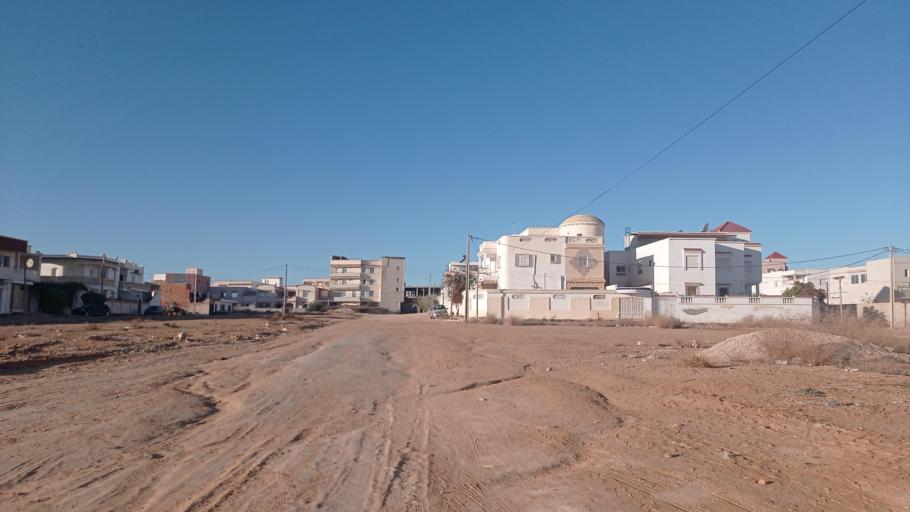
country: TN
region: Qabis
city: Gabes
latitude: 33.8485
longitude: 10.1151
